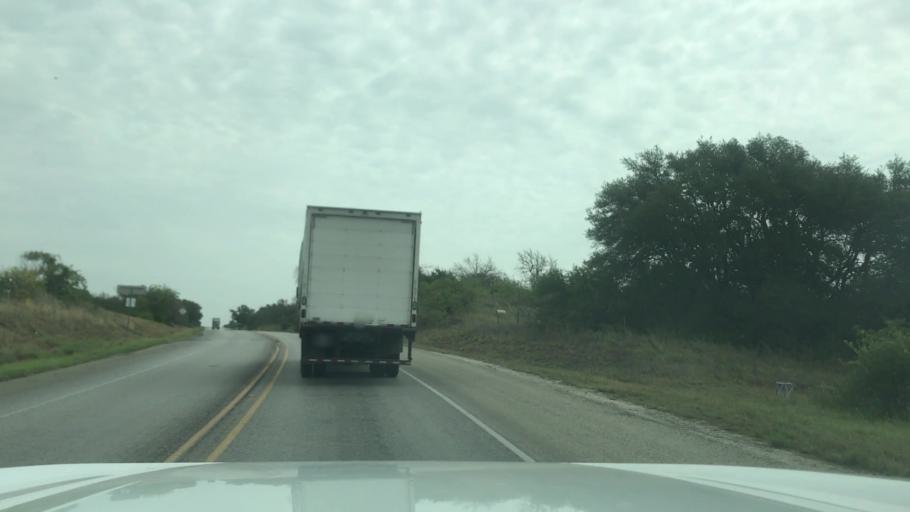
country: US
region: Texas
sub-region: Erath County
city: Dublin
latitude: 32.0876
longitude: -98.4300
